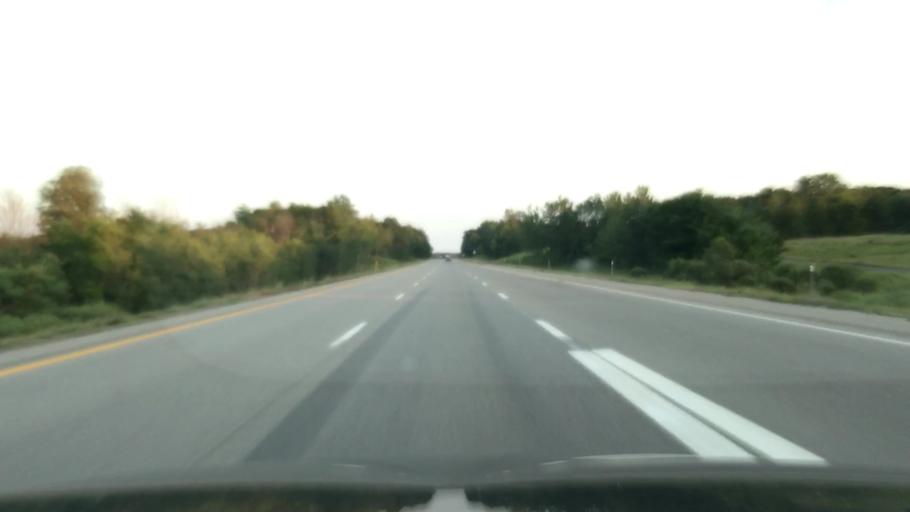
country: US
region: Michigan
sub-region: Montcalm County
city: Howard City
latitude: 43.4848
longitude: -85.4832
